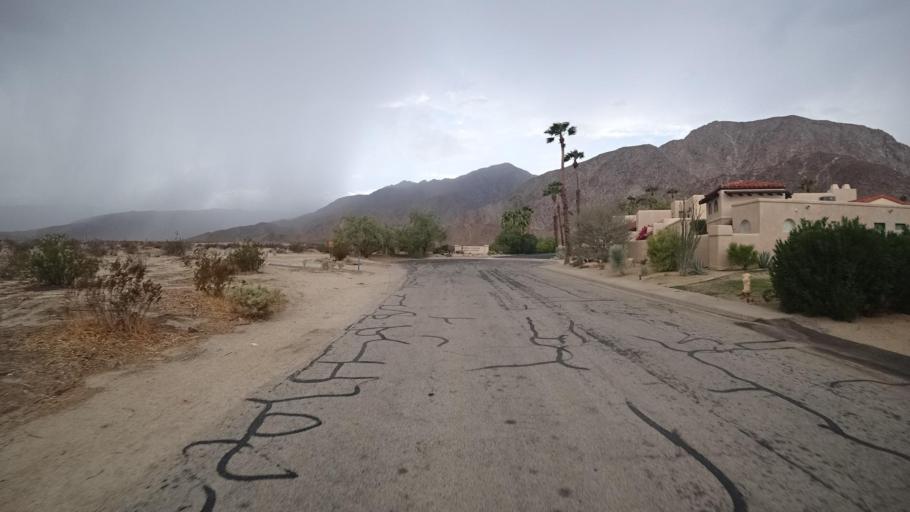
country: US
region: California
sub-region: San Diego County
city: Borrego Springs
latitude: 33.2831
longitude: -116.3950
